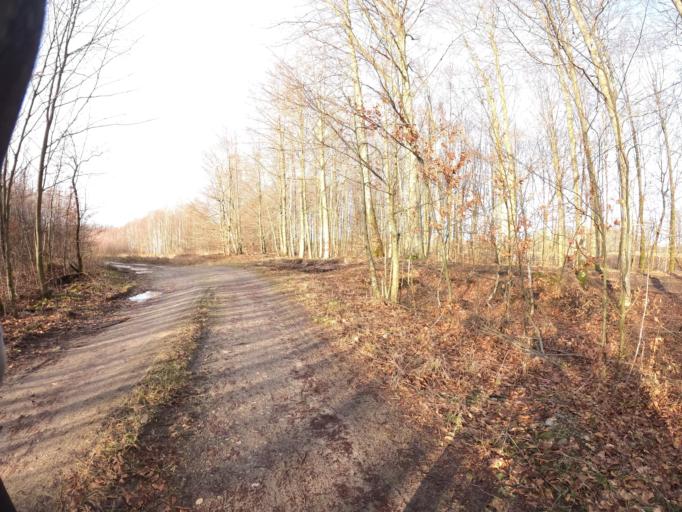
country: PL
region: West Pomeranian Voivodeship
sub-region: Powiat koszalinski
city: Polanow
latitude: 54.1564
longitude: 16.7604
